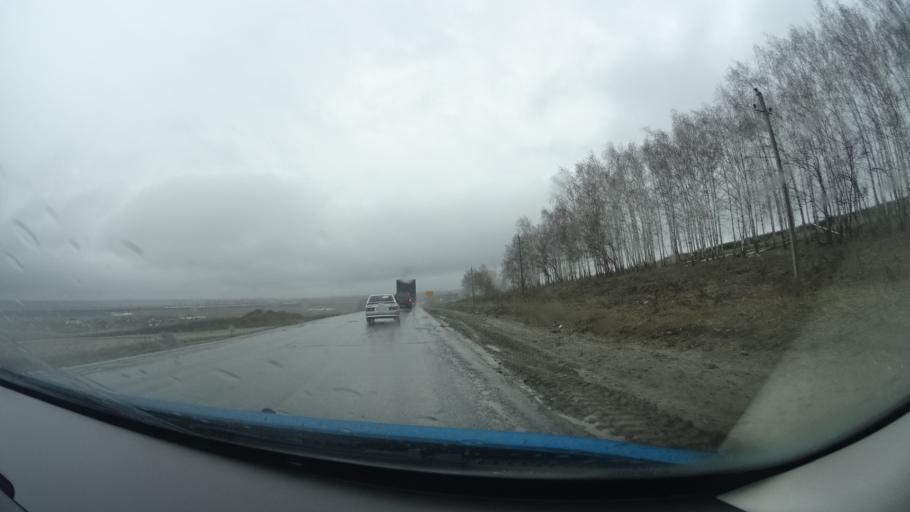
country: RU
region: Bashkortostan
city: Buzdyak
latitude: 54.6347
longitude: 54.4729
